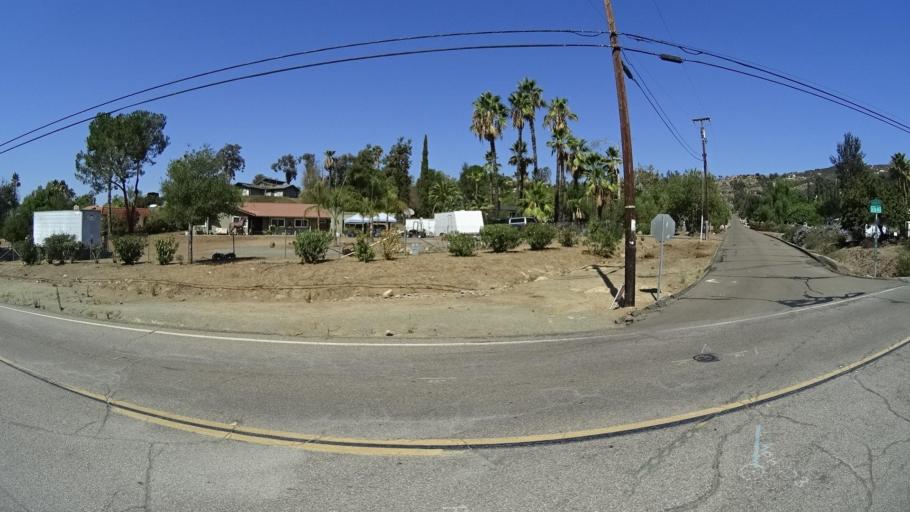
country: US
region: California
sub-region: San Diego County
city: Granite Hills
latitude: 32.8112
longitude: -116.9048
